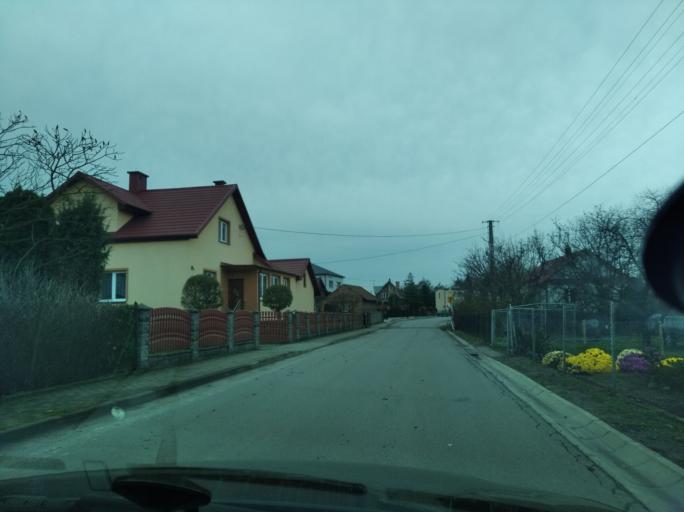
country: PL
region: Subcarpathian Voivodeship
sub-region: Powiat przeworski
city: Debow
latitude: 50.0465
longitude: 22.4247
